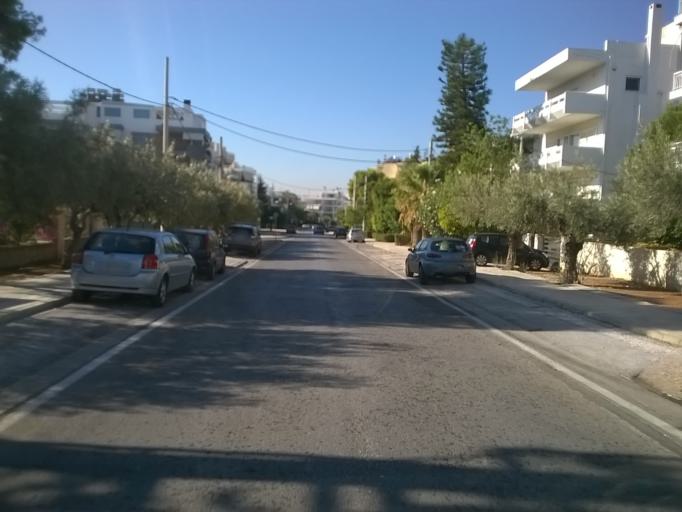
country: GR
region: Attica
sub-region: Nomarchia Athinas
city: Glyfada
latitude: 37.8676
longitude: 23.7527
